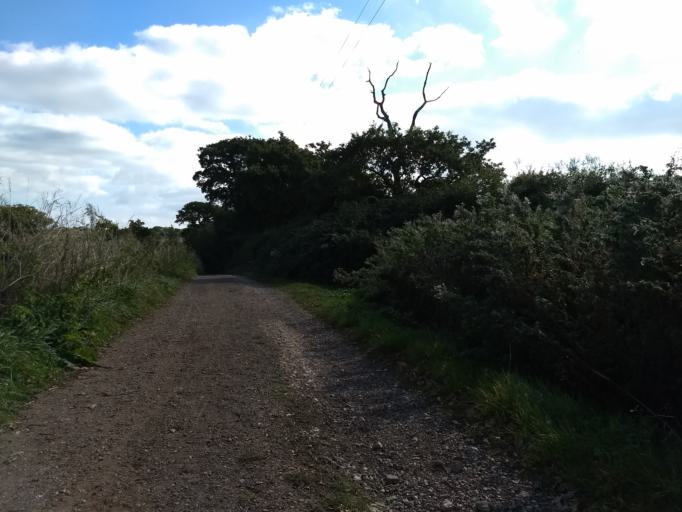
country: GB
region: England
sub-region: Isle of Wight
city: Seaview
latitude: 50.7039
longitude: -1.1233
